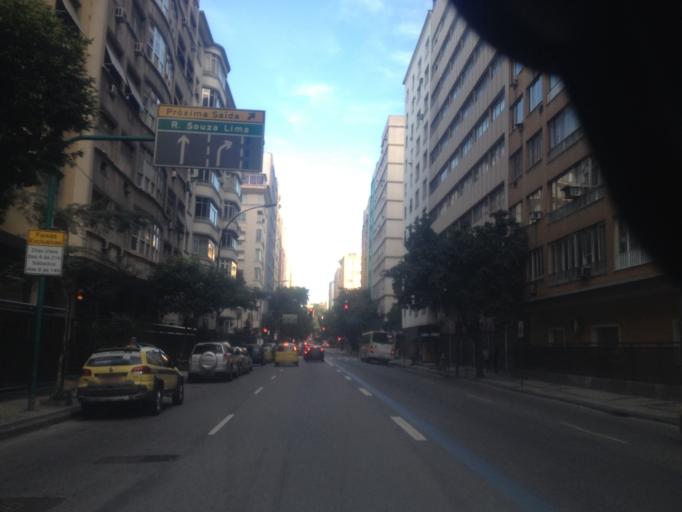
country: BR
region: Rio de Janeiro
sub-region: Rio De Janeiro
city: Rio de Janeiro
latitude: -22.9813
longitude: -43.1924
